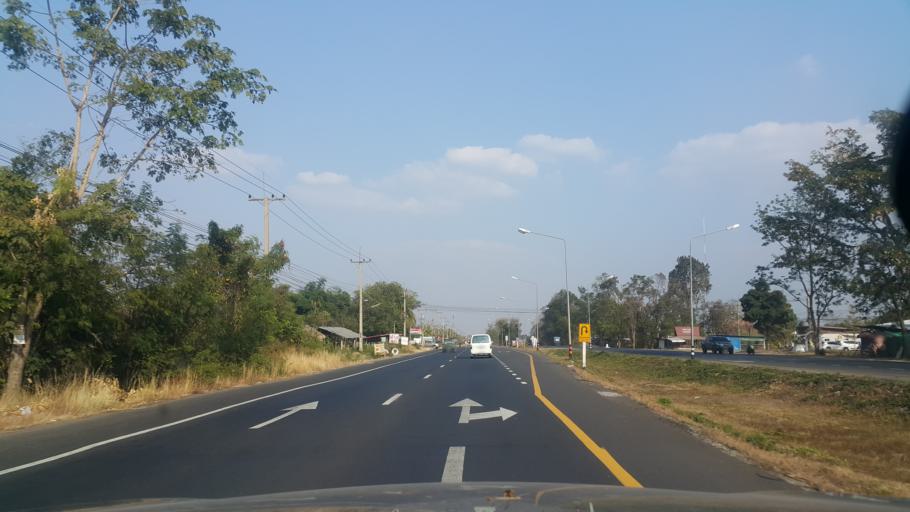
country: TH
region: Buriram
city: Nang Rong
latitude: 14.6341
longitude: 102.7329
